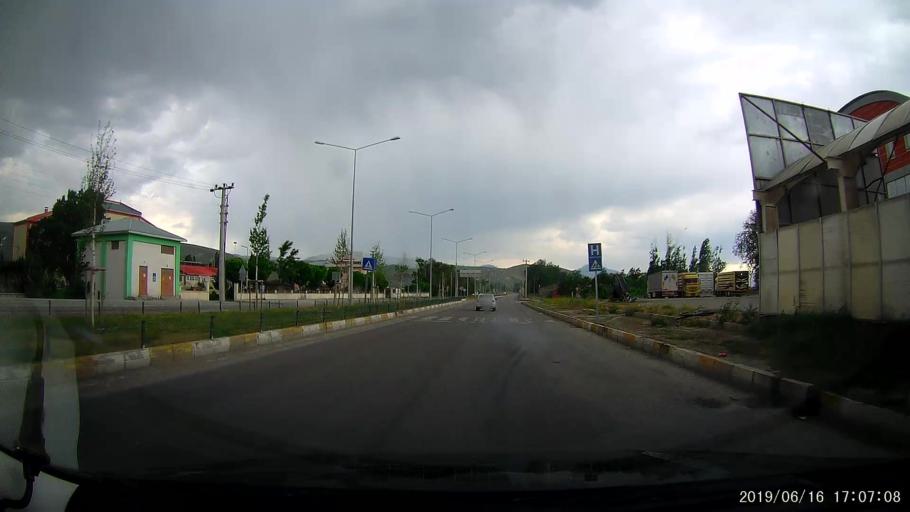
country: TR
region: Erzurum
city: Askale
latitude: 39.9185
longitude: 40.6816
